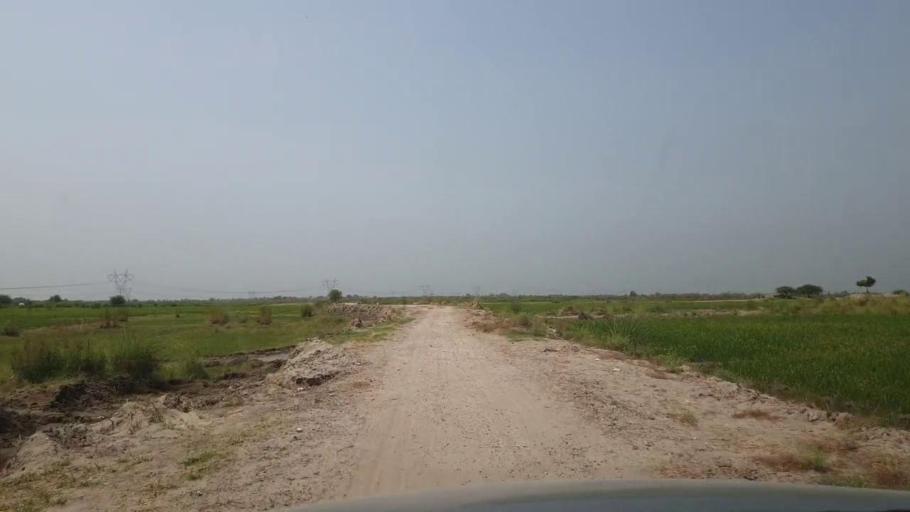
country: PK
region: Sindh
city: Madeji
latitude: 27.8144
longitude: 68.5130
